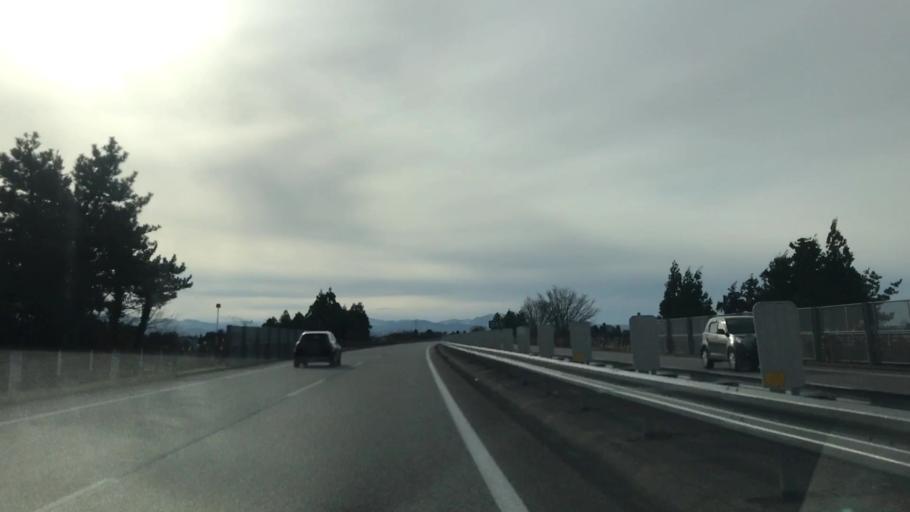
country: JP
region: Toyama
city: Kamiichi
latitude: 36.6765
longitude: 137.3142
